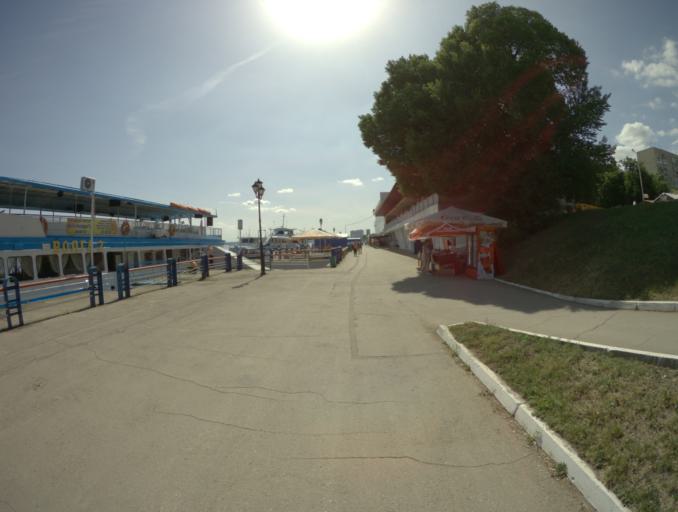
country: RU
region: Saratov
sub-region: Saratovskiy Rayon
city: Saratov
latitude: 51.5253
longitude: 46.0534
